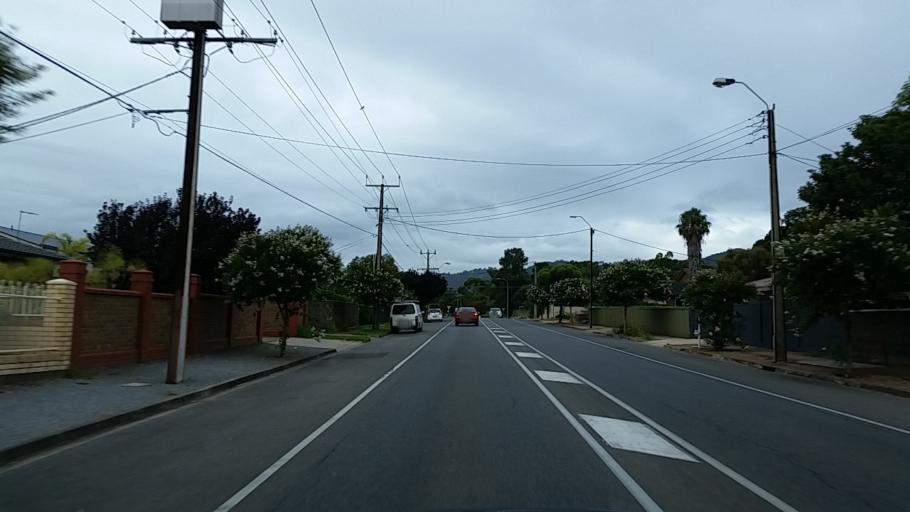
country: AU
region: South Australia
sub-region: Campbelltown
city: Paradise
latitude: -34.8695
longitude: 138.6818
